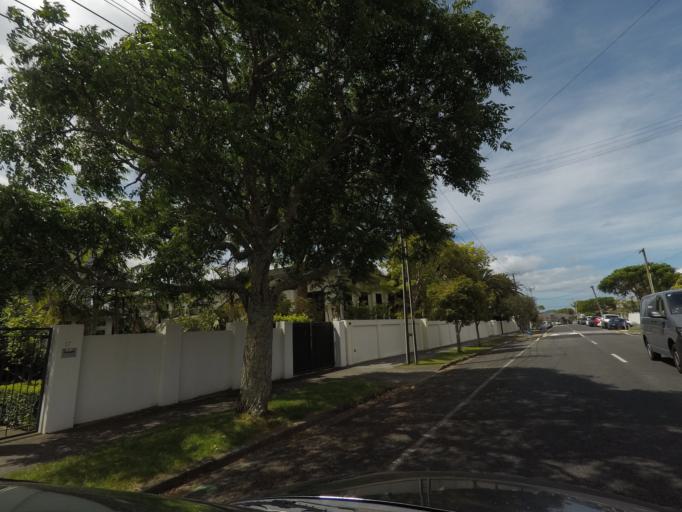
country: NZ
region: Auckland
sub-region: Auckland
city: Auckland
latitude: -36.8434
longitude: 174.7317
